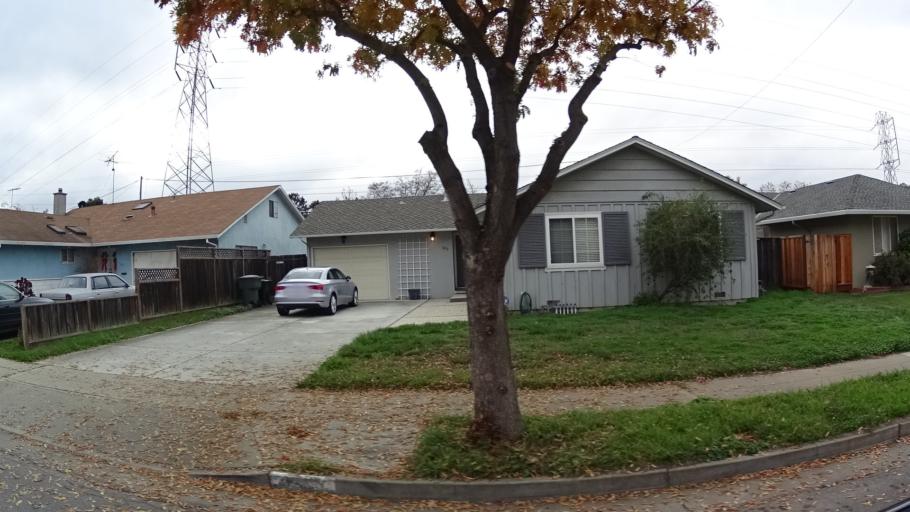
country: US
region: California
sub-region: Santa Clara County
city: Sunnyvale
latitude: 37.3617
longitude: -122.0609
